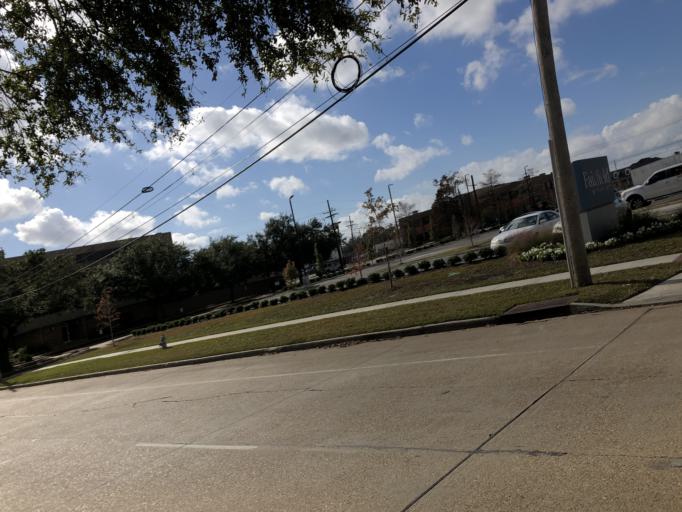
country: US
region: Louisiana
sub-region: Jefferson Parish
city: Metairie
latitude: 30.0003
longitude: -90.1596
